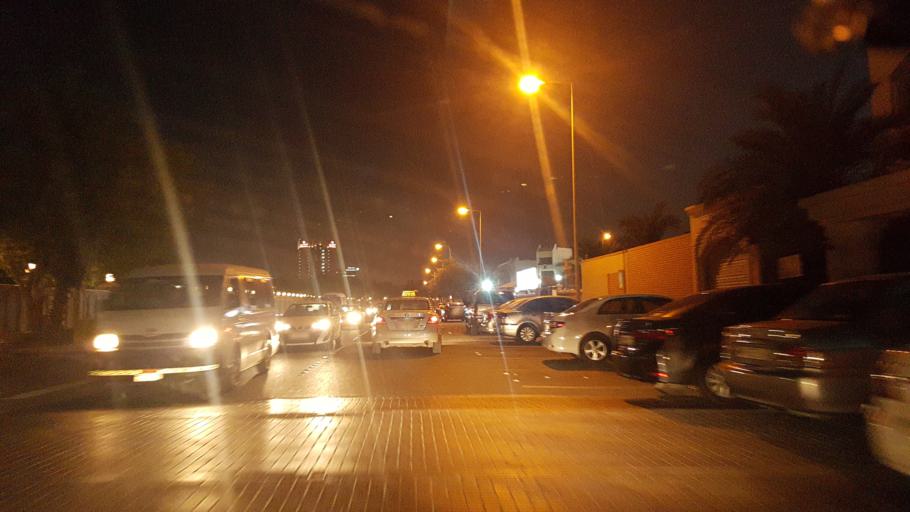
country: BH
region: Manama
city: Manama
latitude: 26.2227
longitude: 50.5949
